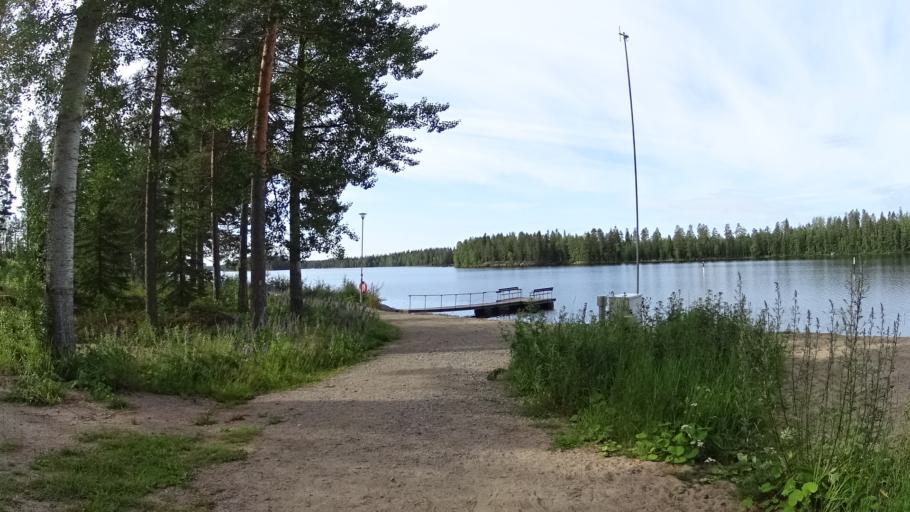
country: FI
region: Southern Ostrobothnia
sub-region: Kuusiokunnat
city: AEhtaeri
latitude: 62.5347
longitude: 24.1807
